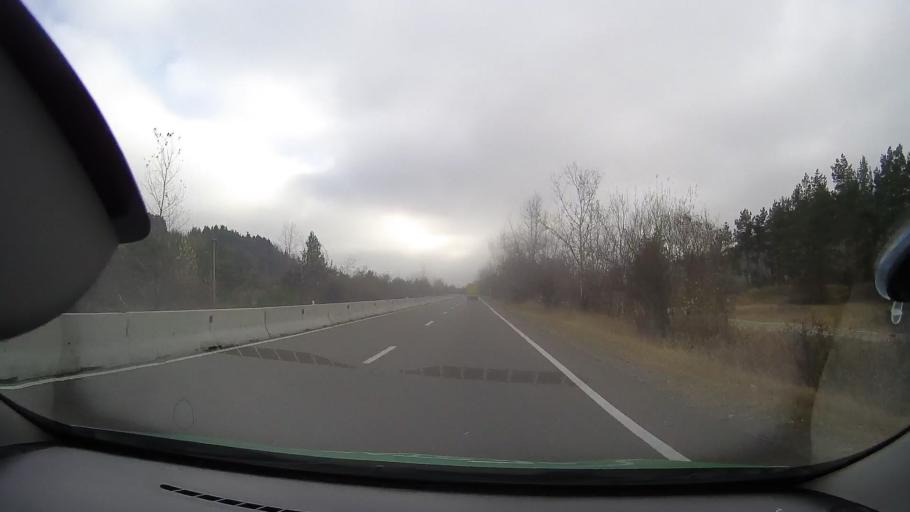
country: RO
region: Prahova
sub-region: Municipiul Campina
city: Campina
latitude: 45.1135
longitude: 25.7349
